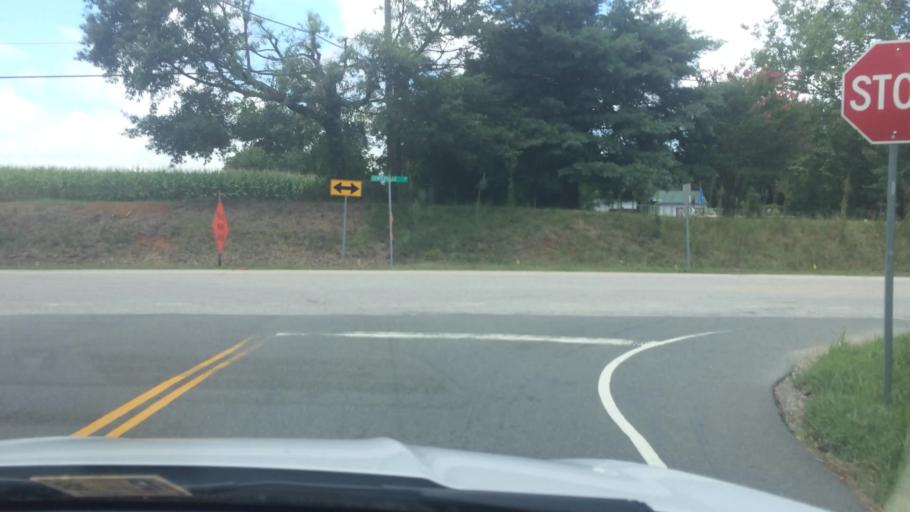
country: US
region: Virginia
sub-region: James City County
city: Williamsburg
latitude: 37.2814
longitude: -76.8045
